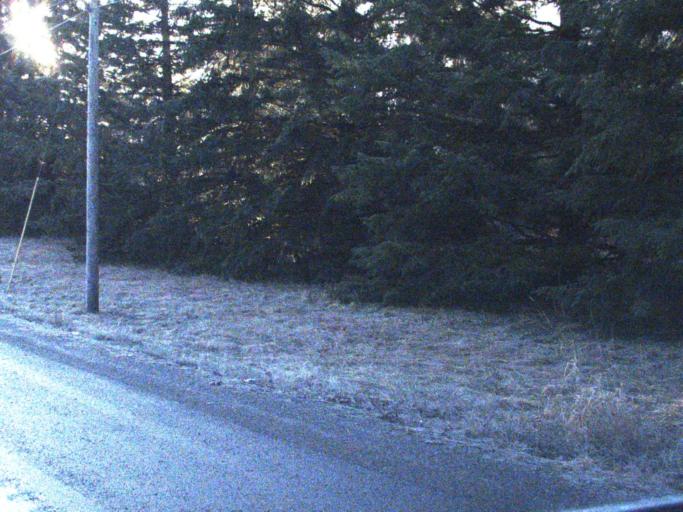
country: US
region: Washington
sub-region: Snohomish County
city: Darrington
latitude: 48.4924
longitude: -121.6358
